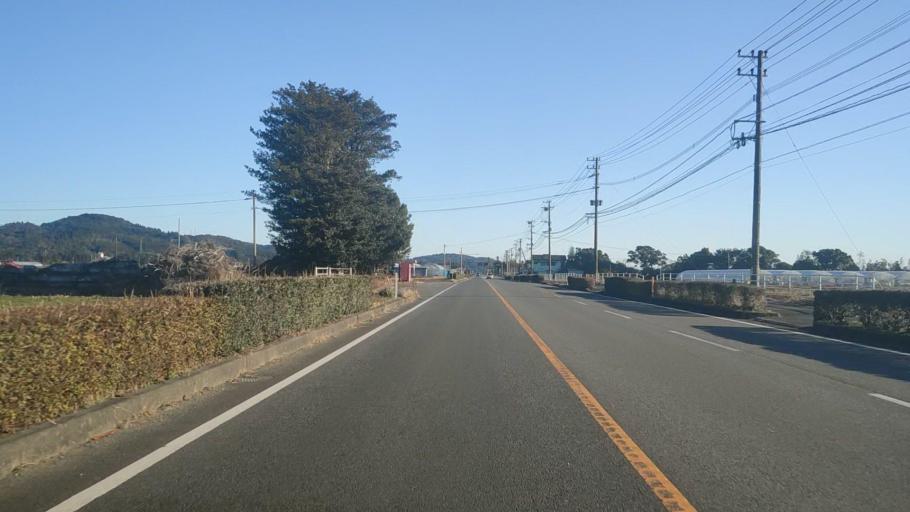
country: JP
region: Miyazaki
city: Takanabe
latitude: 32.3189
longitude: 131.5930
